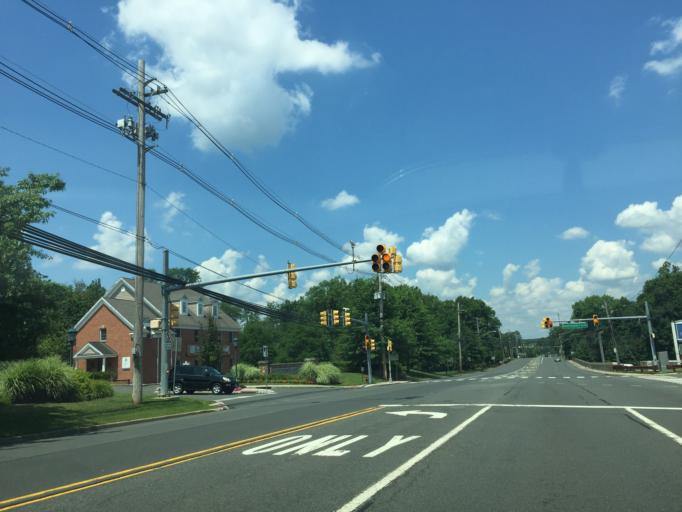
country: US
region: New Jersey
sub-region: Somerset County
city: Martinsville
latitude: 40.6527
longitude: -74.5756
